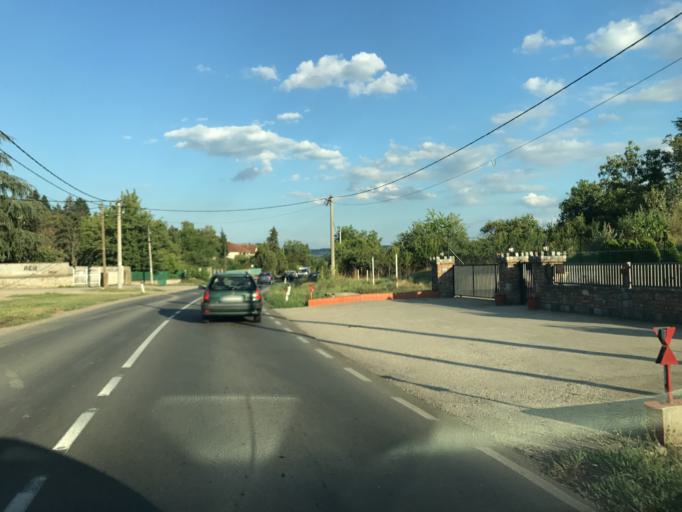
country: RS
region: Central Serbia
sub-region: Belgrade
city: Grocka
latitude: 44.6870
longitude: 20.7002
